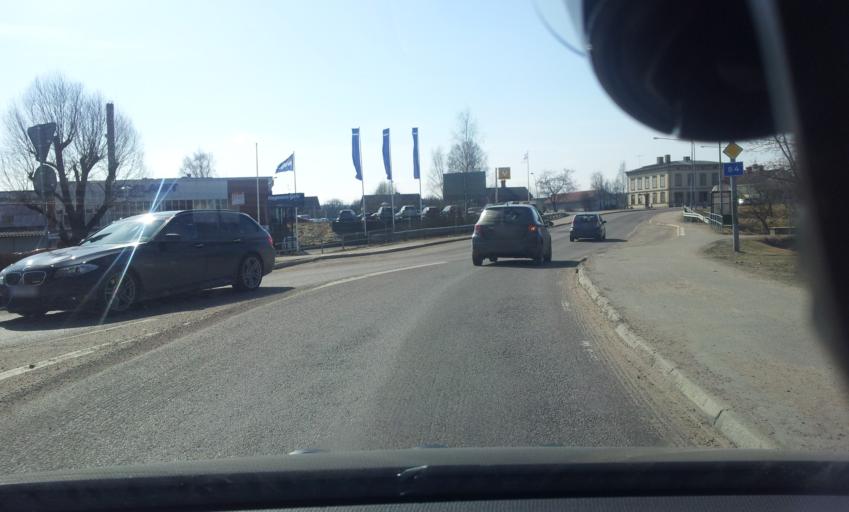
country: SE
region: Gaevleborg
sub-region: Ljusdals Kommun
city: Ljusdal
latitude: 61.8291
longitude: 16.0816
